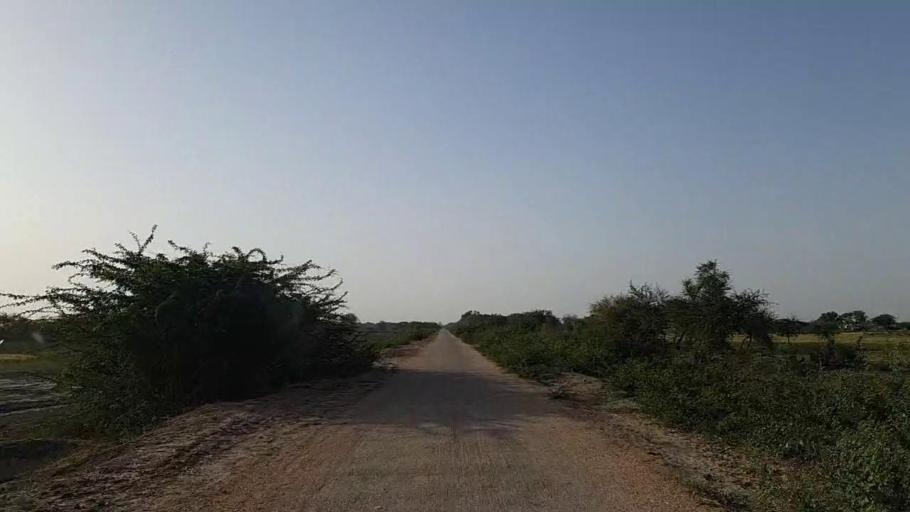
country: PK
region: Sindh
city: Jati
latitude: 24.3341
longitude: 68.1552
